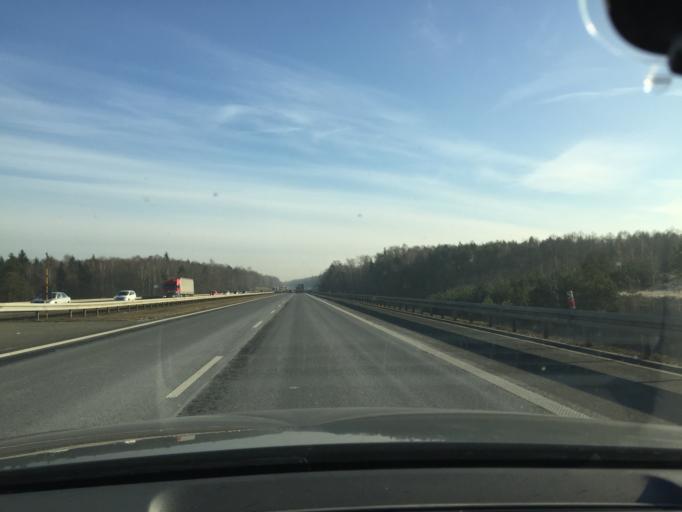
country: PL
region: Silesian Voivodeship
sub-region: Katowice
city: Murcki
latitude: 50.2264
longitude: 19.0811
